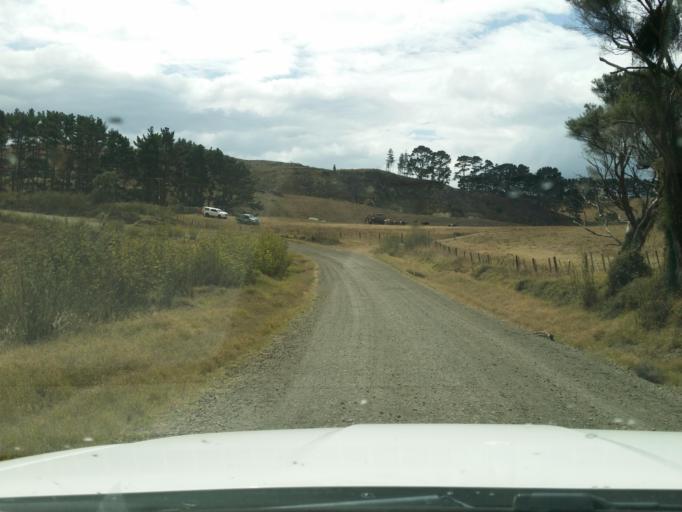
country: NZ
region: Auckland
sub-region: Auckland
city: Wellsford
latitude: -36.3326
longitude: 174.1554
